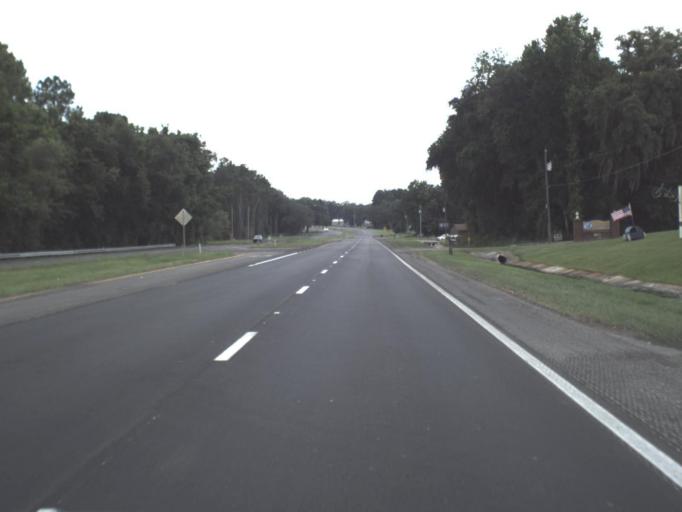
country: US
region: Florida
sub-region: Columbia County
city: Lake City
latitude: 30.1609
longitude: -82.6426
